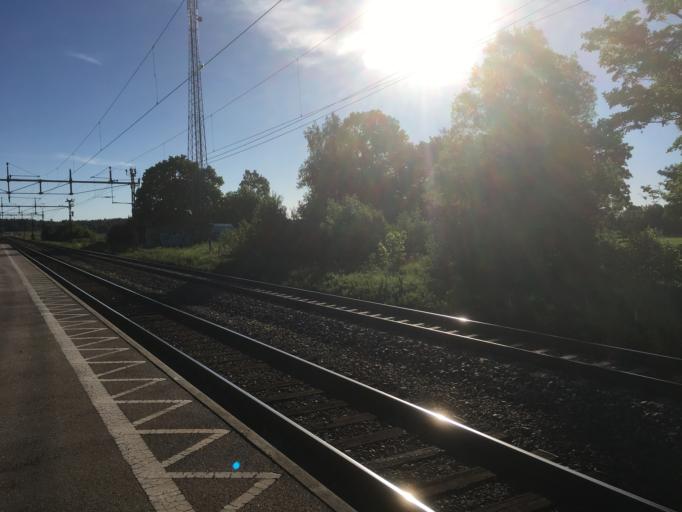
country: SE
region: Gaevleborg
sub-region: Hofors Kommun
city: Hofors
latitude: 60.5131
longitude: 16.4877
